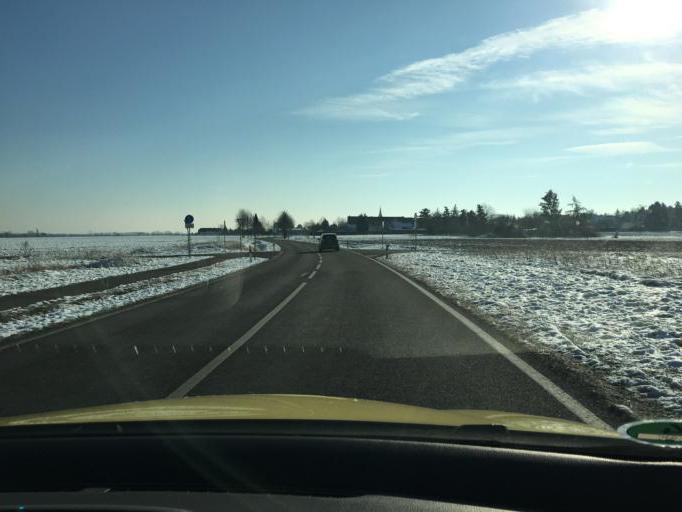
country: DE
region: Saxony
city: Grossposna
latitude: 51.2877
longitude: 12.5239
